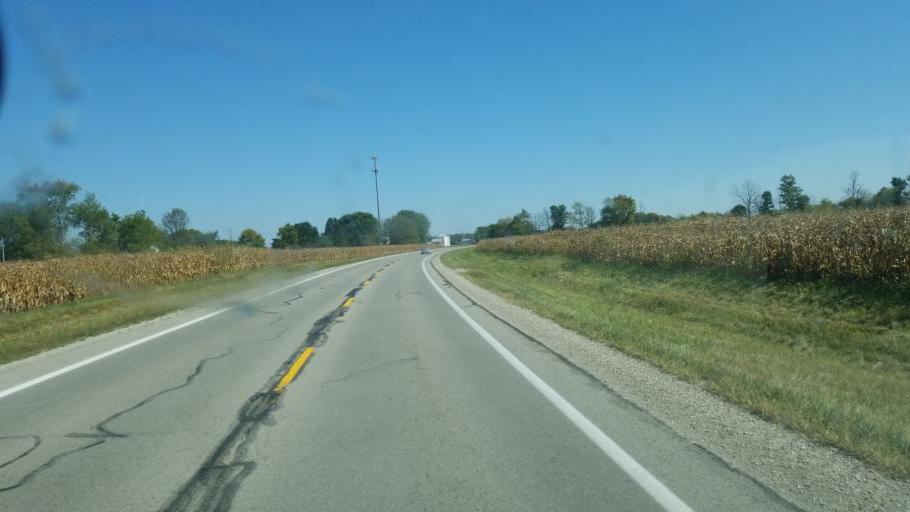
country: US
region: Ohio
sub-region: Morrow County
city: Cardington
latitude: 40.6366
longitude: -82.9558
